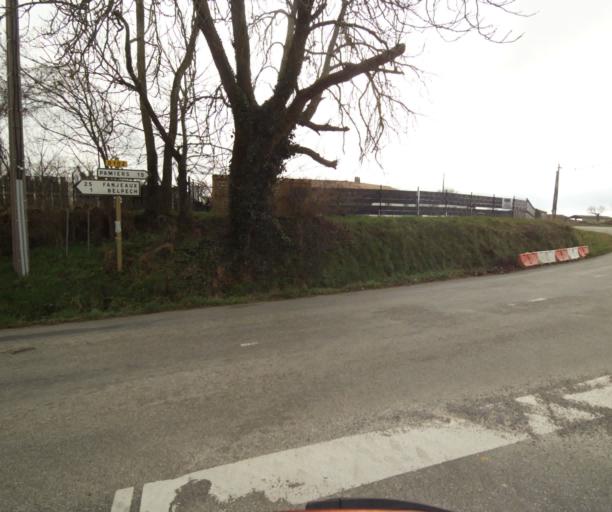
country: FR
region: Languedoc-Roussillon
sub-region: Departement de l'Aude
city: Belpech
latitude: 43.2006
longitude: 1.7347
